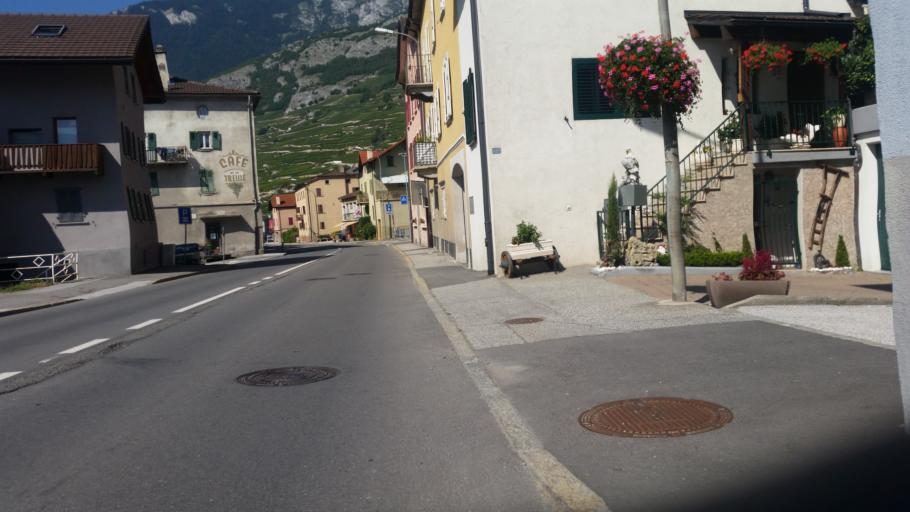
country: CH
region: Valais
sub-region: Conthey District
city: Vetroz
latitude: 46.2258
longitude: 7.2828
